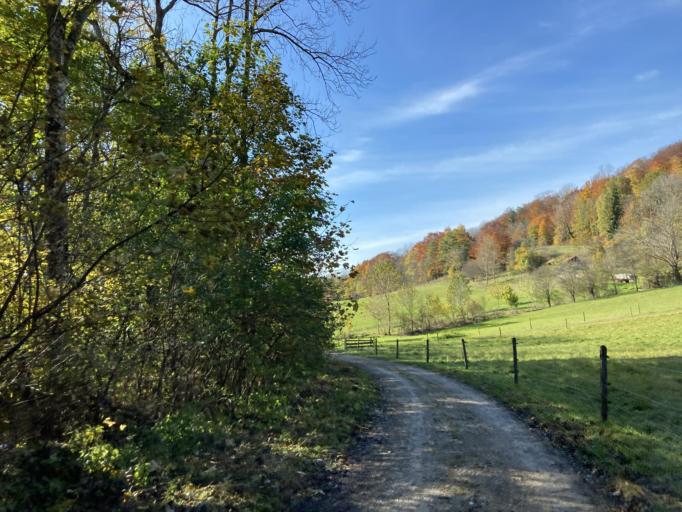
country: DE
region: Baden-Wuerttemberg
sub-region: Tuebingen Region
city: Nehren
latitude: 48.3948
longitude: 9.1198
